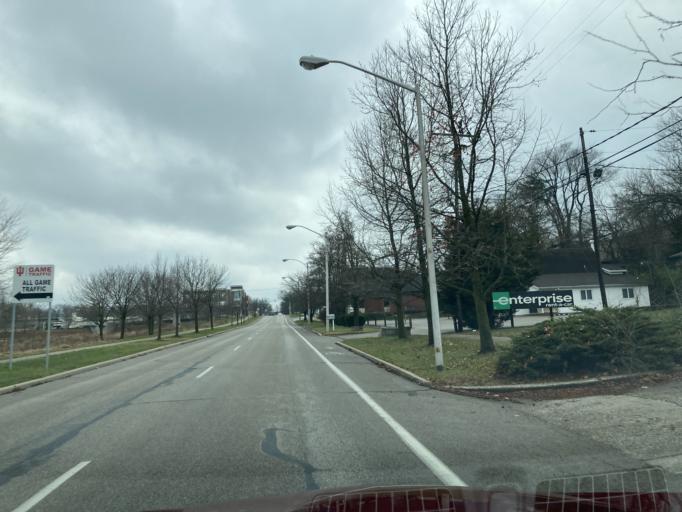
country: US
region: Indiana
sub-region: Monroe County
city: Bloomington
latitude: 39.1812
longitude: -86.5347
